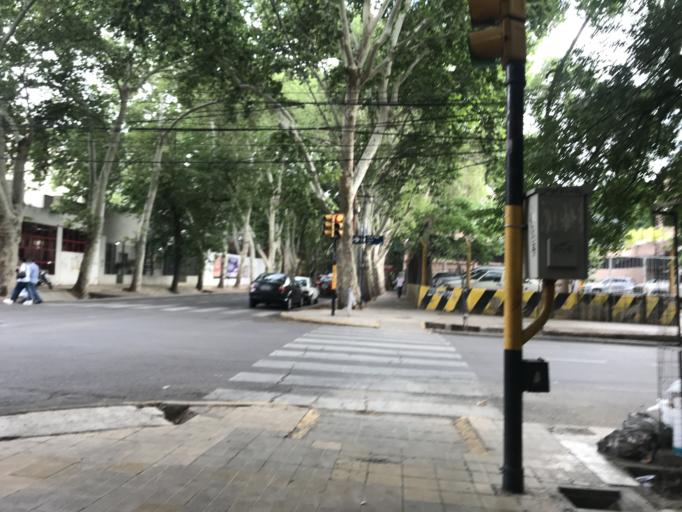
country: AR
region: Mendoza
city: Mendoza
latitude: -32.8843
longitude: -68.8443
